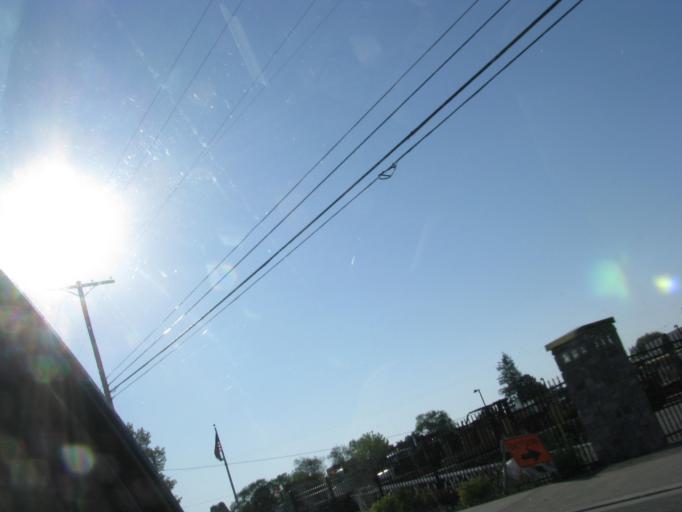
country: US
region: Washington
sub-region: Spokane County
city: Veradale
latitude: 47.6574
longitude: -117.1679
